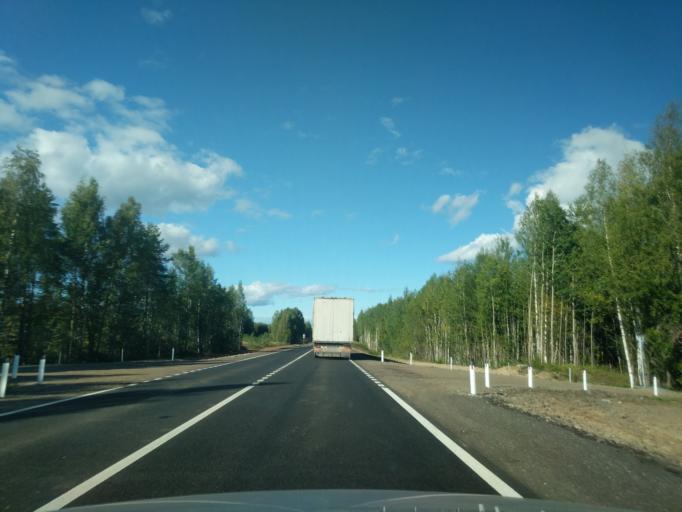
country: RU
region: Kostroma
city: Makar'yev
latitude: 57.9893
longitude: 43.9657
